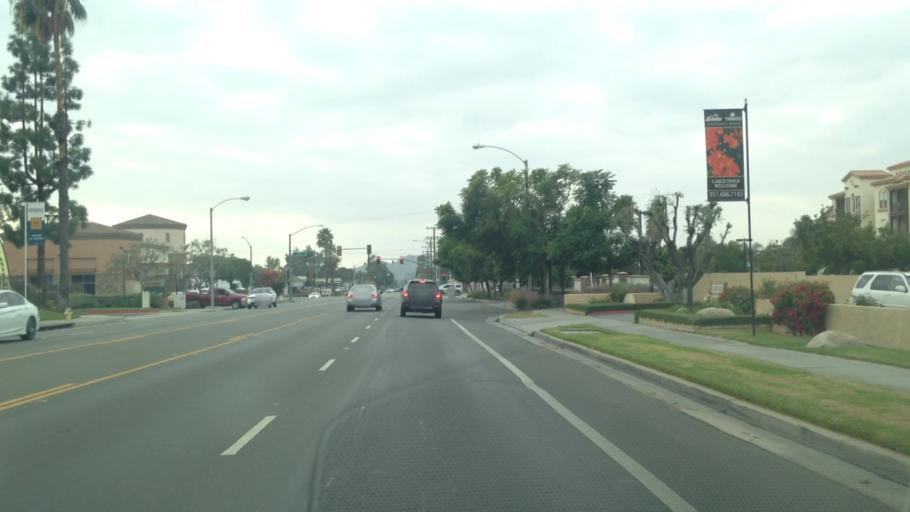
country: US
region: California
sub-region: Riverside County
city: Highgrove
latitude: 33.9831
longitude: -117.3382
